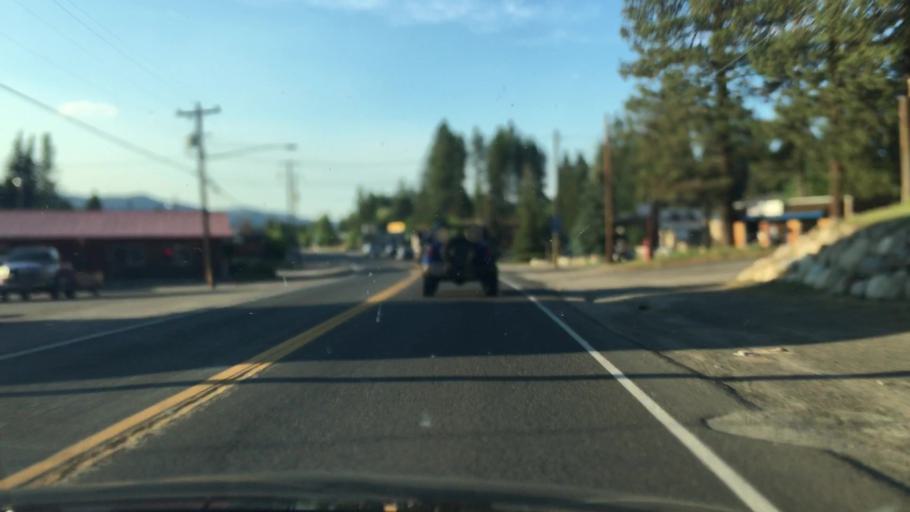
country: US
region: Idaho
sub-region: Valley County
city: McCall
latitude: 44.9046
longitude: -116.0979
